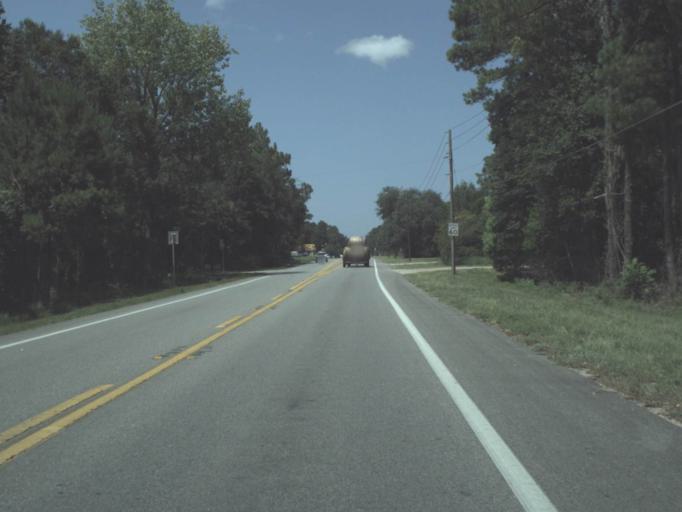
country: US
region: Florida
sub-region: Taylor County
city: Perry
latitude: 30.1059
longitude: -83.6053
